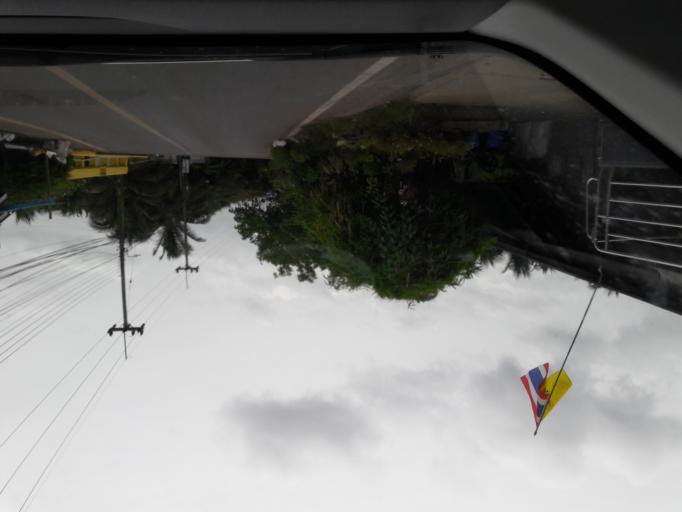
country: TH
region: Samut Sakhon
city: Ban Phaeo
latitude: 13.6015
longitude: 100.0240
